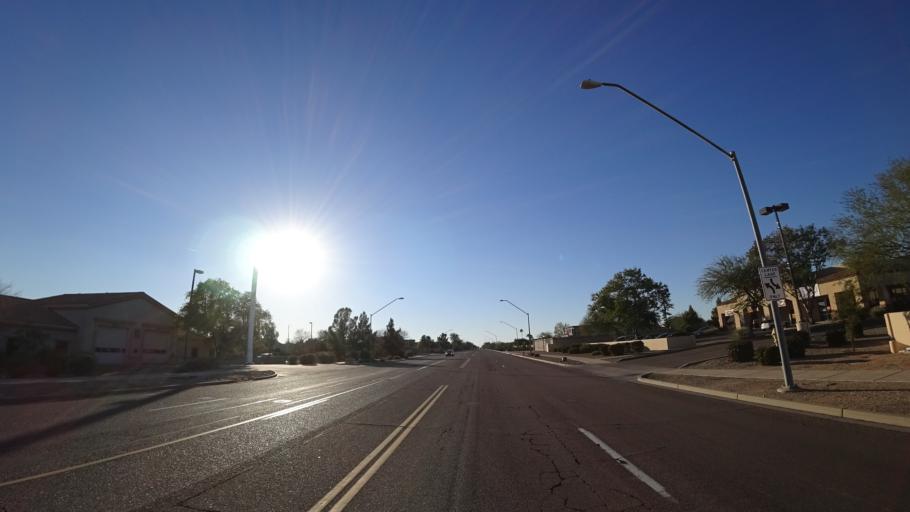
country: US
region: Arizona
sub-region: Maricopa County
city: Peoria
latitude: 33.6819
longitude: -112.2052
